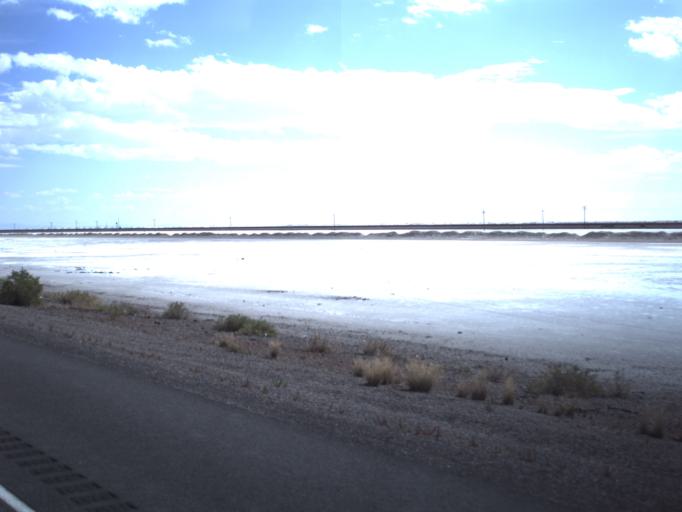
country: US
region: Utah
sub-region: Tooele County
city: Wendover
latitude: 40.7398
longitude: -113.9186
